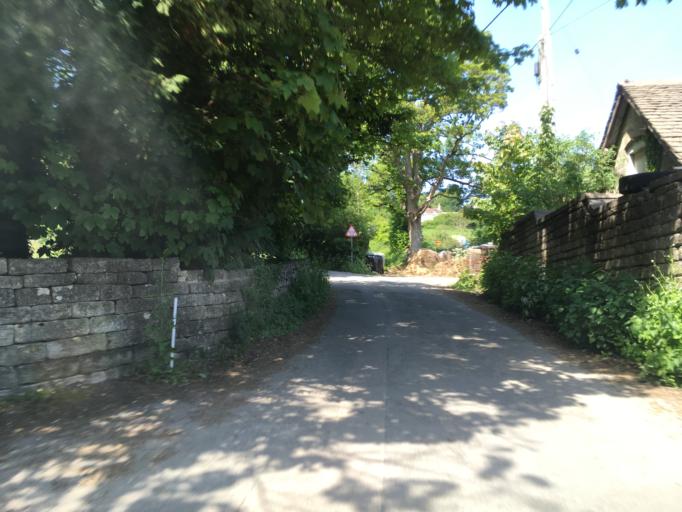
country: GB
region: England
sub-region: Gloucestershire
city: Minchinhampton
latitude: 51.6934
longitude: -2.1937
